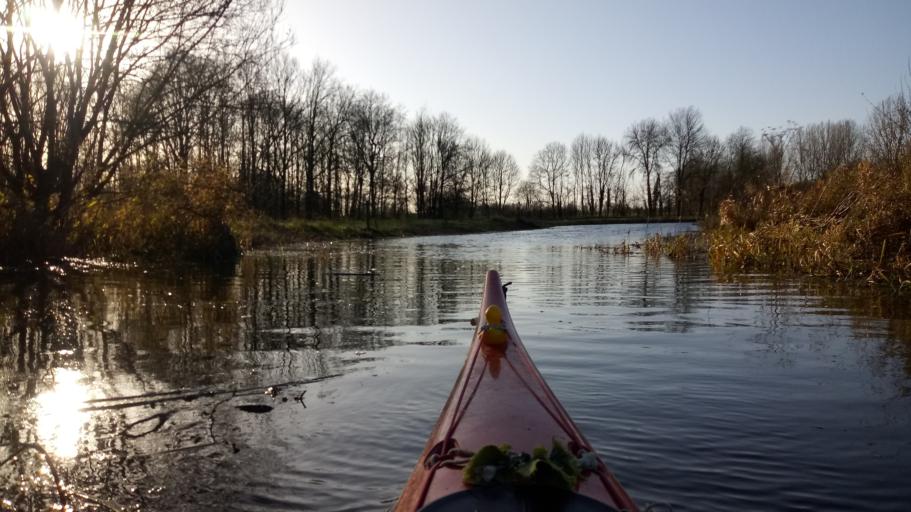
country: NL
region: Gelderland
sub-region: Gemeente Bronckhorst
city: Baak
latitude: 52.0971
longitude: 6.2654
